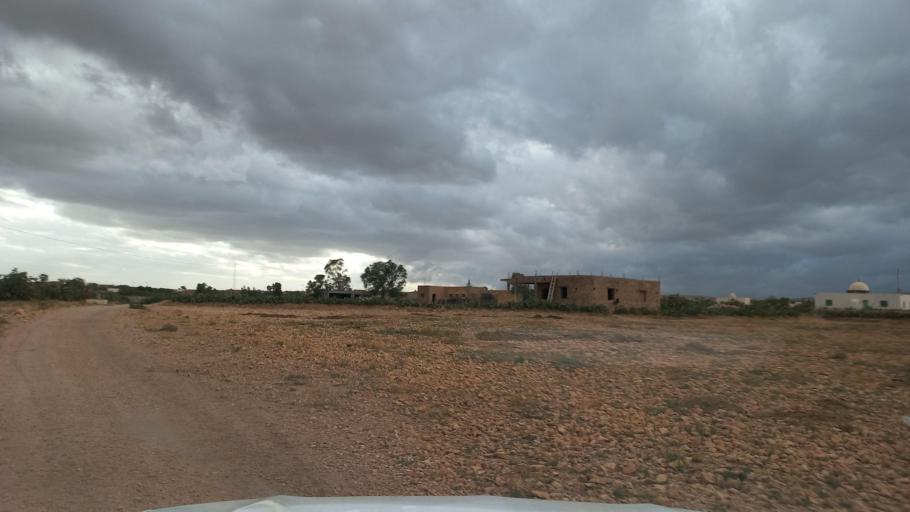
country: TN
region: Al Qasrayn
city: Kasserine
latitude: 35.2796
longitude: 8.9518
